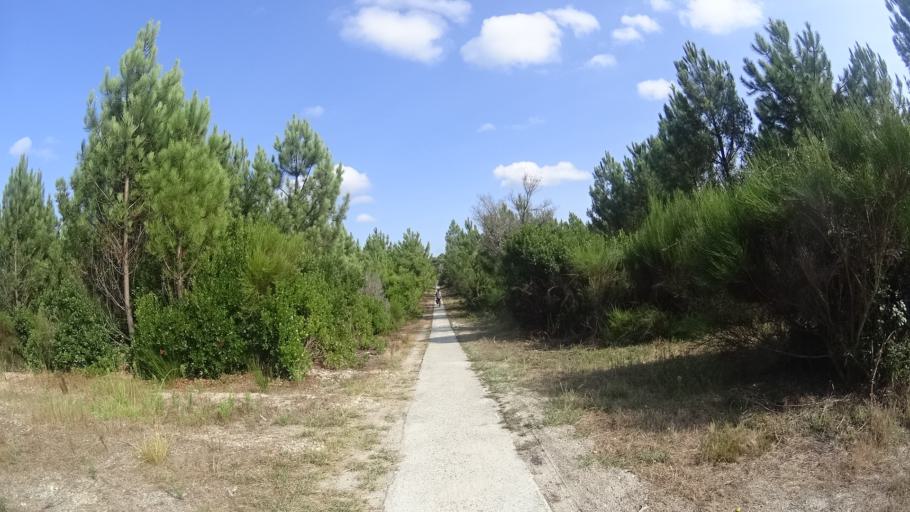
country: FR
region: Aquitaine
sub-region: Departement de la Gironde
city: Lacanau
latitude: 44.9660
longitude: -1.1776
